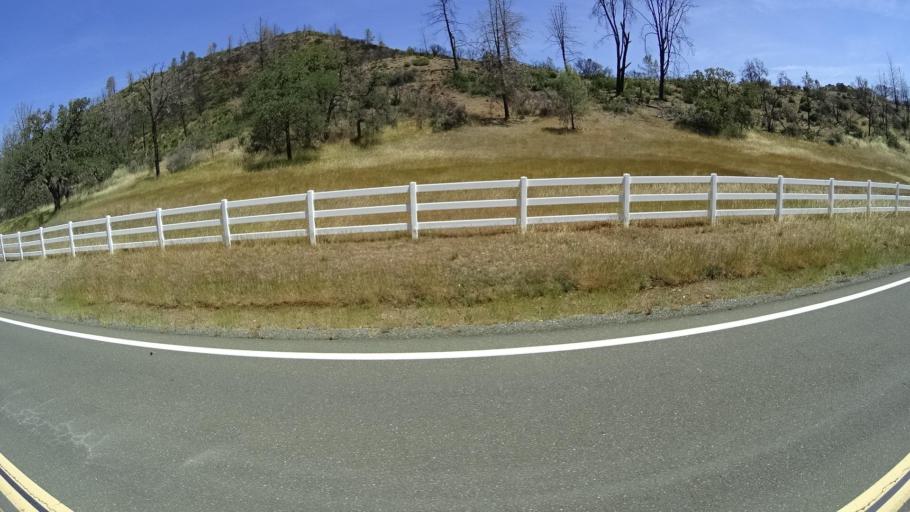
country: US
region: California
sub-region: Lake County
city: Hidden Valley Lake
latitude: 38.7198
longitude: -122.5008
